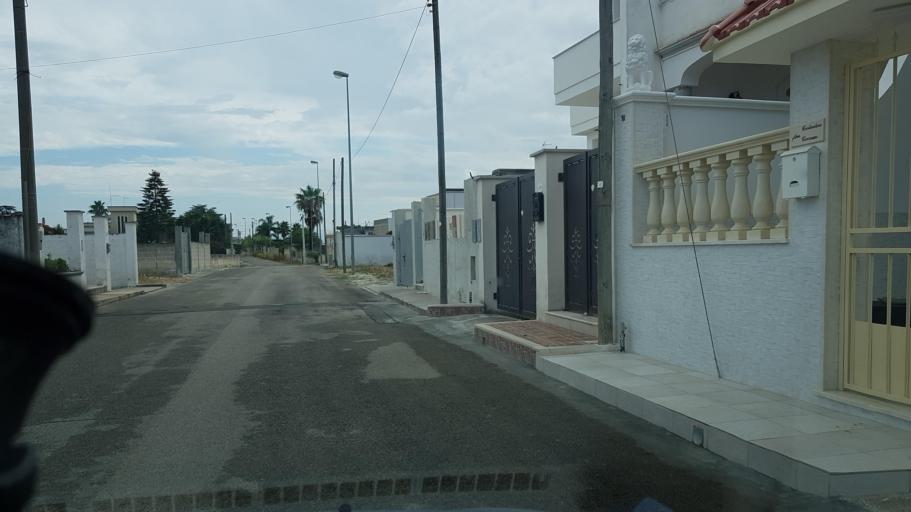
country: IT
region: Apulia
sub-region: Provincia di Brindisi
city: Torre Santa Susanna
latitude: 40.4738
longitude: 17.7420
